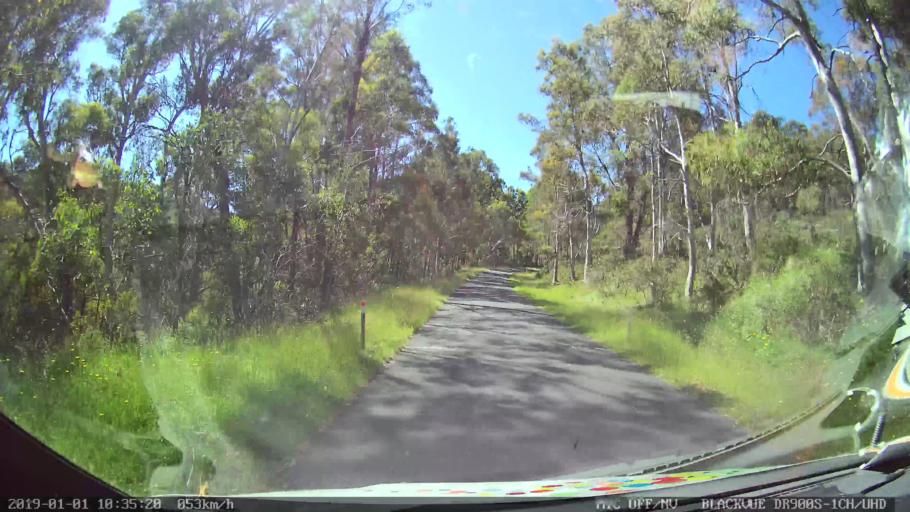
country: AU
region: New South Wales
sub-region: Snowy River
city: Jindabyne
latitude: -36.0468
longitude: 148.2886
